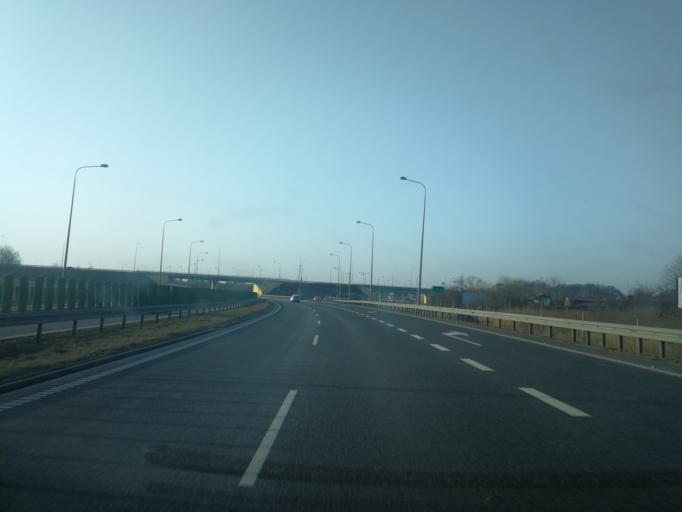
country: PL
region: Warmian-Masurian Voivodeship
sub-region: Powiat elblaski
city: Gronowo Gorne
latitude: 54.1363
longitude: 19.4533
